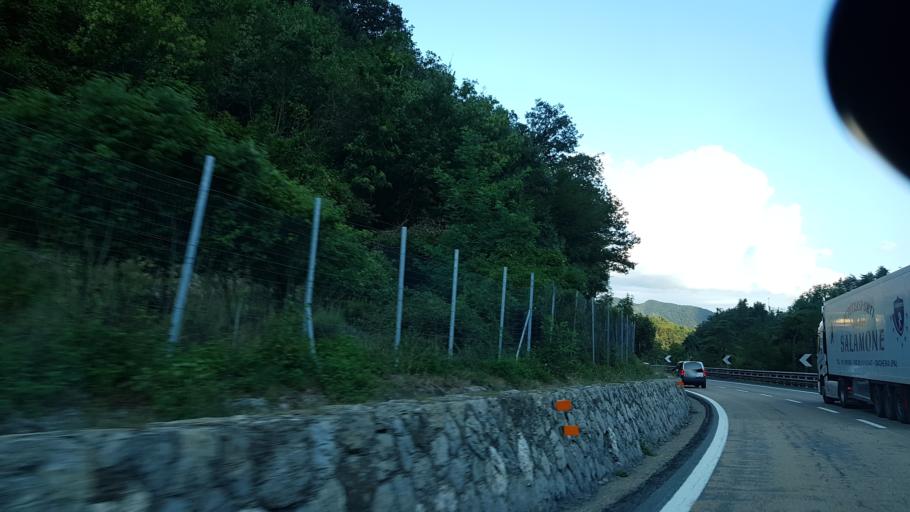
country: IT
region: Liguria
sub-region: Provincia di Genova
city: Isola del Cantone
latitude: 44.6515
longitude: 8.9495
